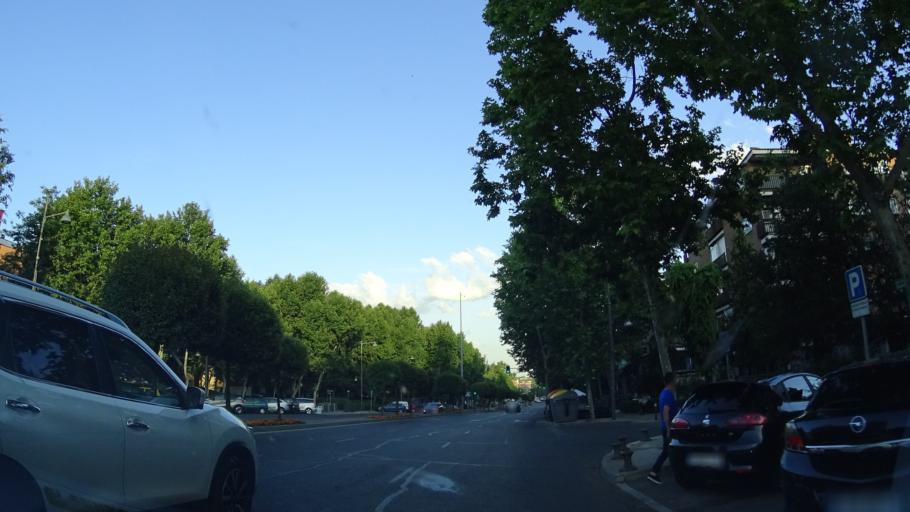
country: ES
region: Madrid
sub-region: Provincia de Madrid
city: Alcobendas
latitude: 40.5428
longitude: -3.6432
